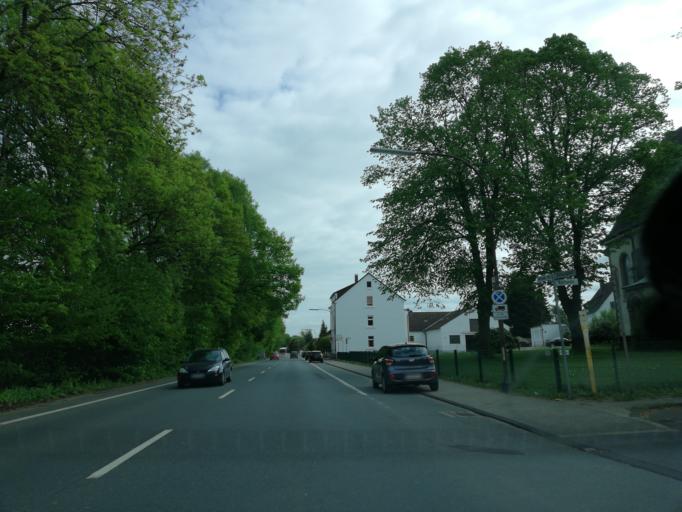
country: DE
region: North Rhine-Westphalia
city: Sprockhovel
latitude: 51.3369
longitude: 7.2850
